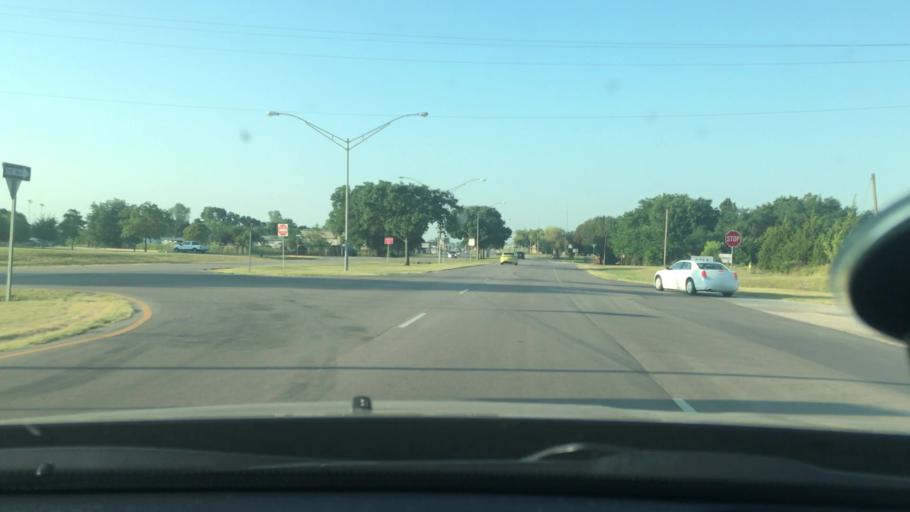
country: US
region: Oklahoma
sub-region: Pontotoc County
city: Ada
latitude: 34.8014
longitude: -96.6786
